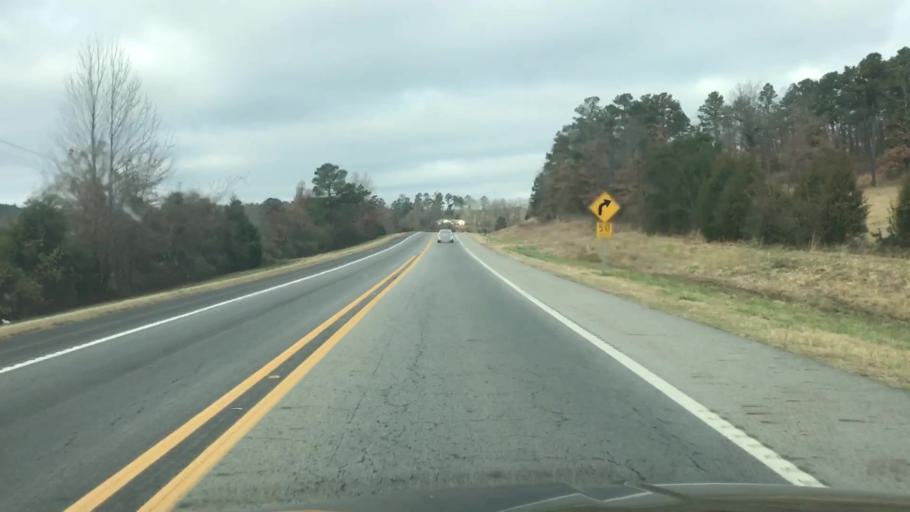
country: US
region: Arkansas
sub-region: Scott County
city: Waldron
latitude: 34.8386
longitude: -94.0495
